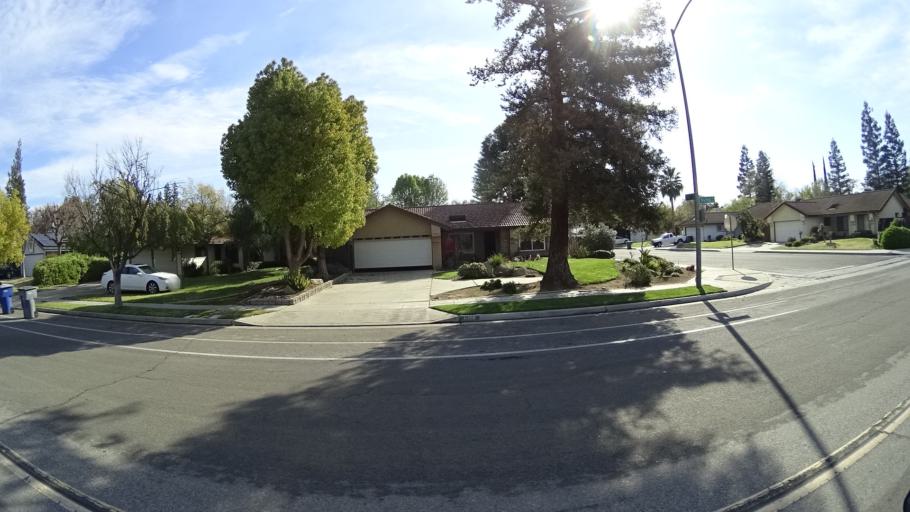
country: US
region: California
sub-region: Fresno County
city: West Park
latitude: 36.8315
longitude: -119.8716
